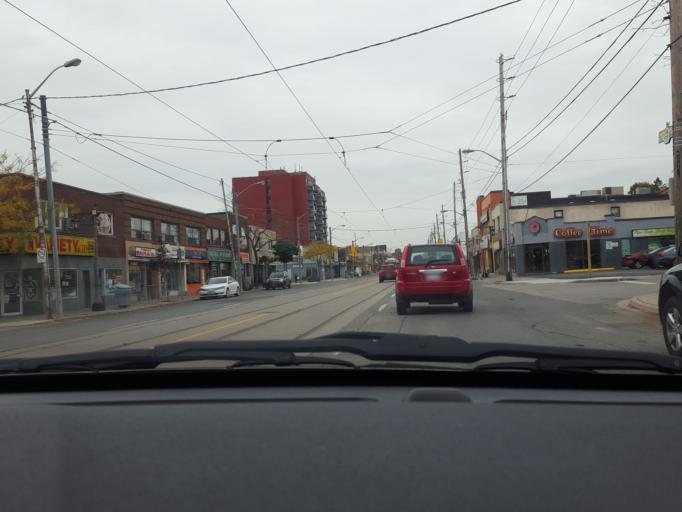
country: CA
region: Ontario
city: Etobicoke
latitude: 43.6021
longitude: -79.4992
